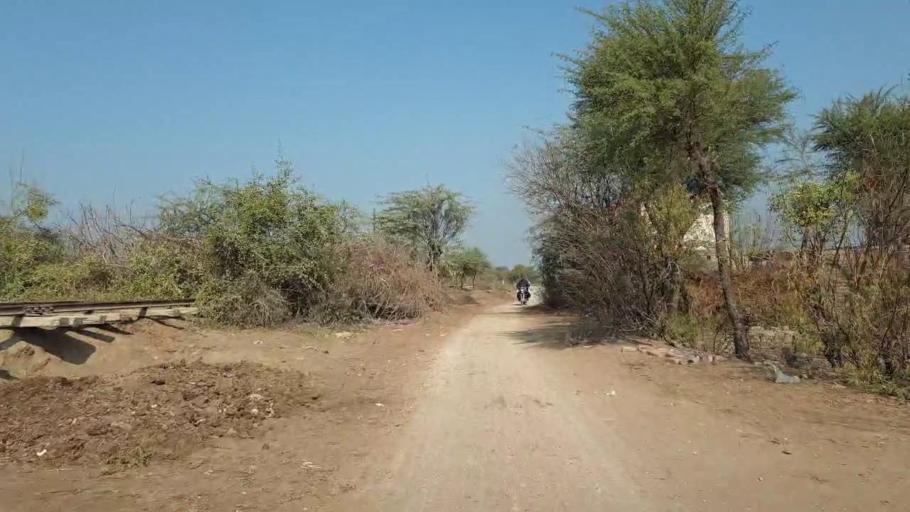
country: PK
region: Sindh
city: Hala
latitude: 25.8879
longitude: 68.4033
